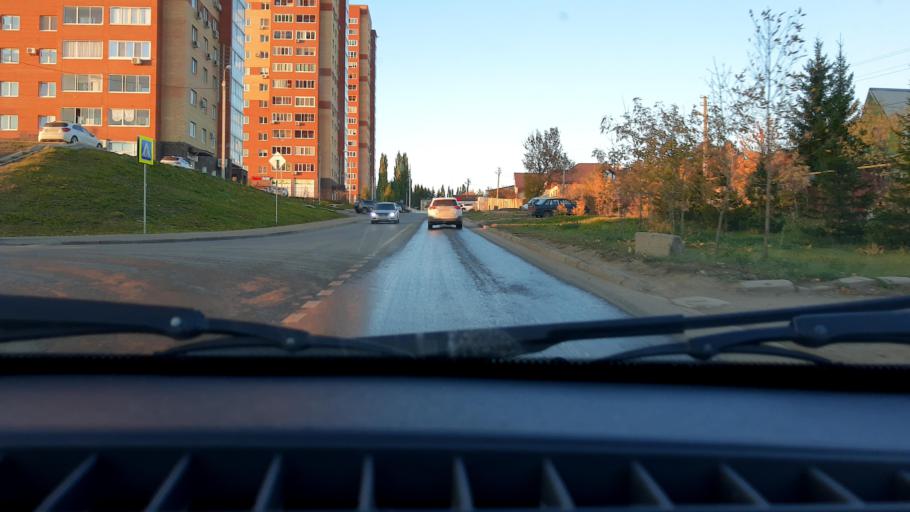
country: RU
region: Bashkortostan
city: Ufa
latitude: 54.6886
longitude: 55.9979
